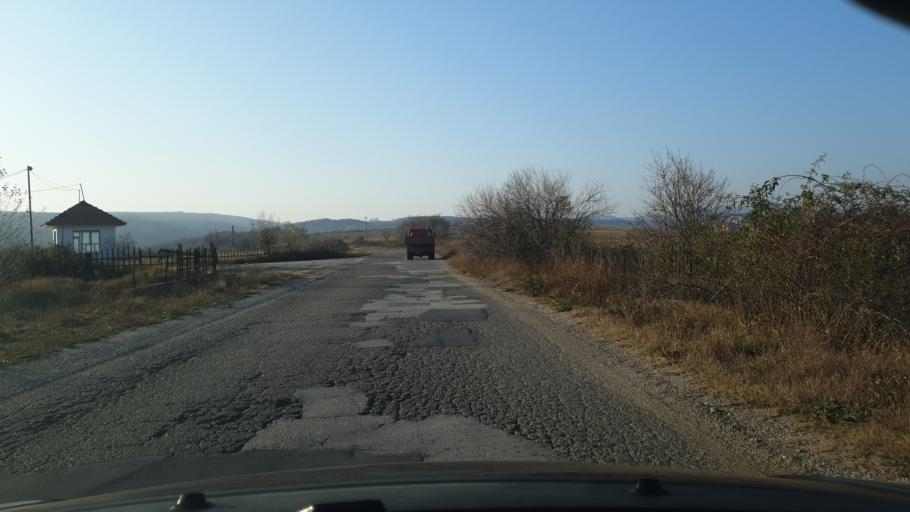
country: RS
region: Central Serbia
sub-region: Zajecarski Okrug
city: Zajecar
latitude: 44.0926
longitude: 22.3375
